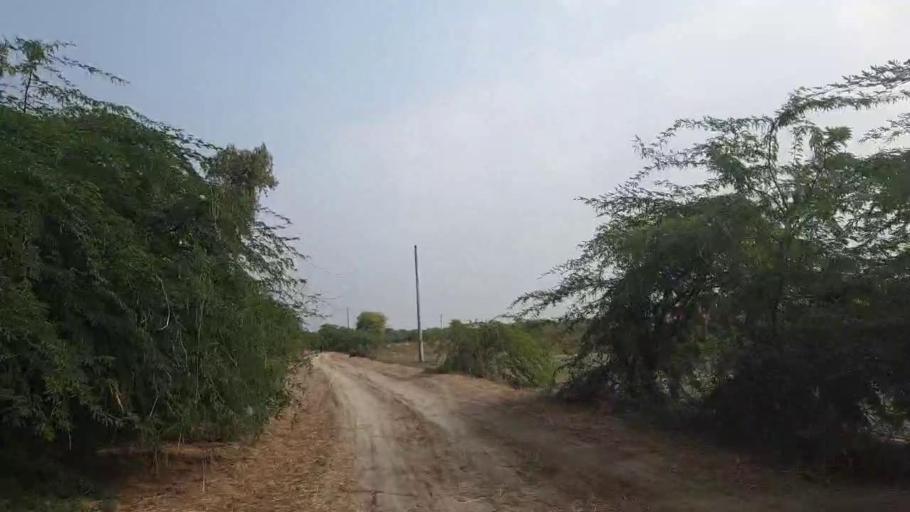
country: PK
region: Sindh
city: Badin
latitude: 24.7663
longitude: 68.8015
